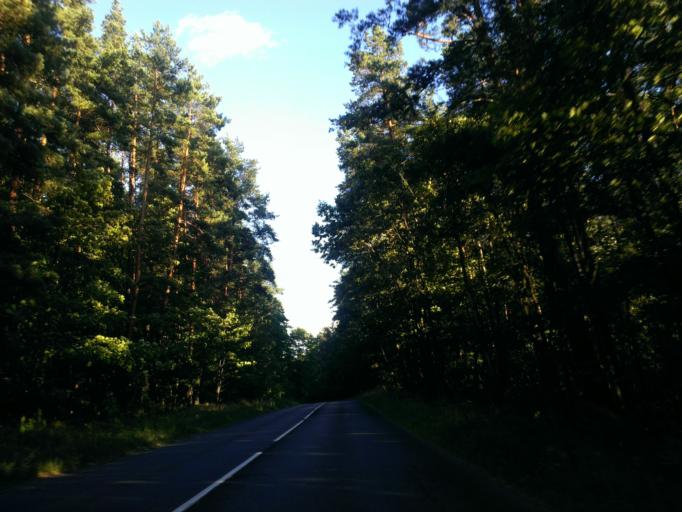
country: LV
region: Riga
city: Bergi
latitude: 57.0071
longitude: 24.2462
